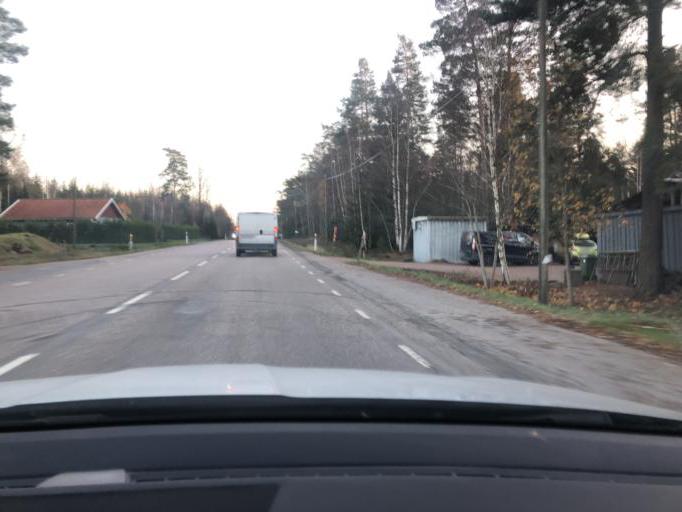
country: SE
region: Soedermanland
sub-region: Strangnas Kommun
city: Akers Styckebruk
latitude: 59.2995
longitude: 17.0995
